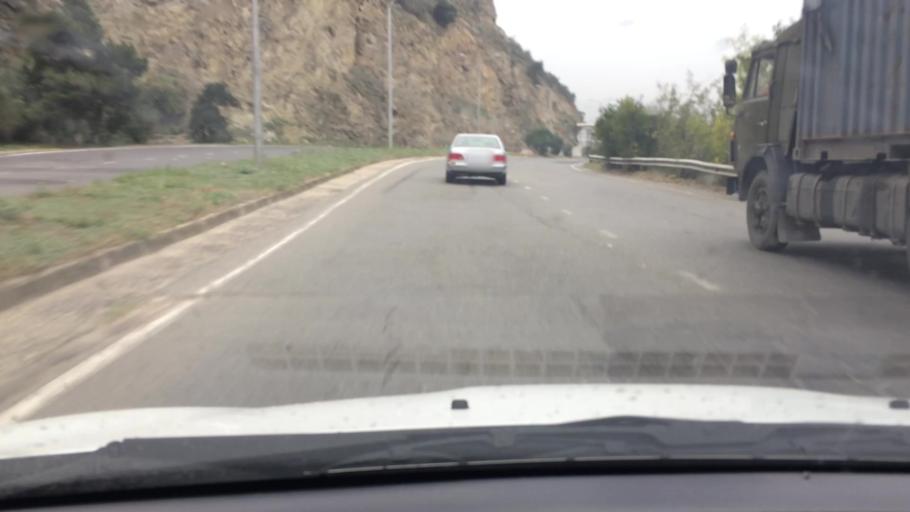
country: GE
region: T'bilisi
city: Tbilisi
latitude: 41.6581
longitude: 44.8917
